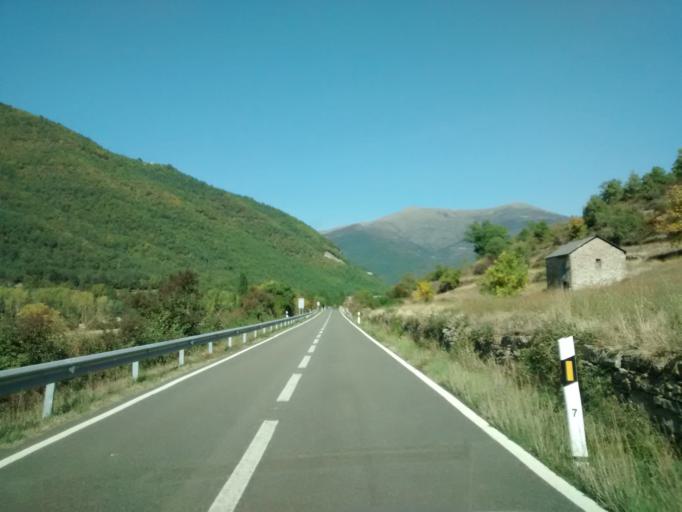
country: ES
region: Aragon
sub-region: Provincia de Huesca
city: Fiscal
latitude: 42.5067
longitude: -0.1237
